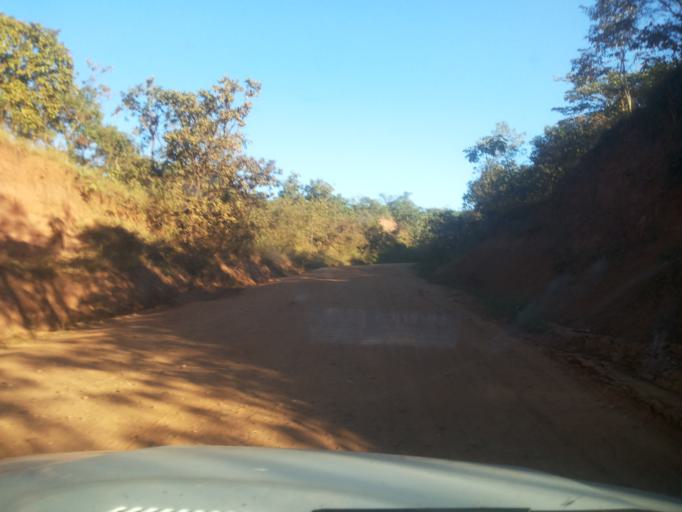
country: BR
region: Minas Gerais
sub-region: Campina Verde
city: Campina Verde
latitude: -19.3258
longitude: -49.7998
